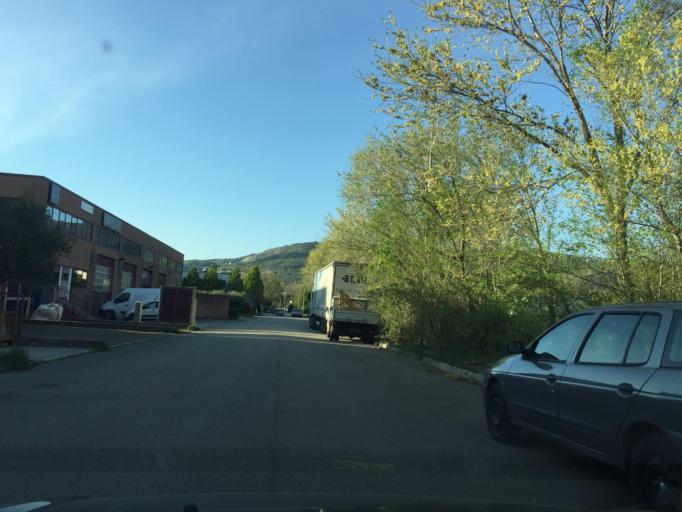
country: IT
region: Friuli Venezia Giulia
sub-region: Provincia di Trieste
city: Dolina
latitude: 45.6024
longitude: 13.8517
